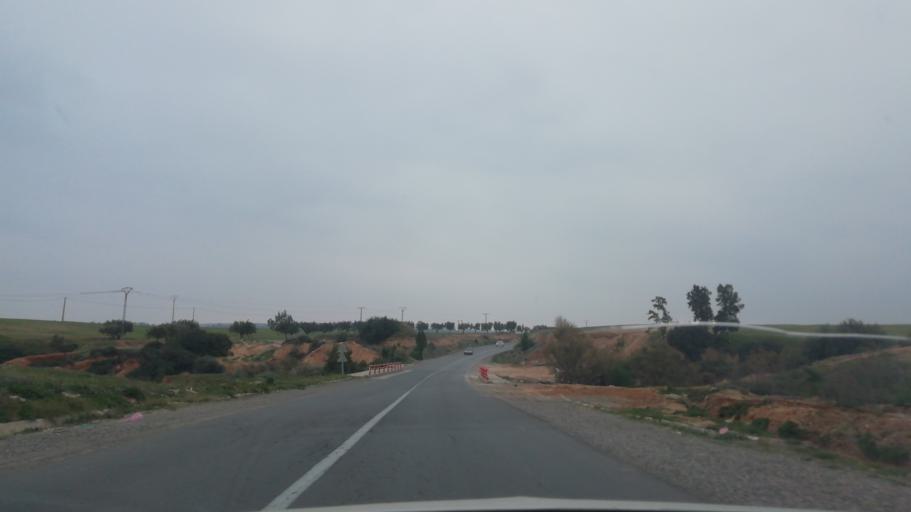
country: DZ
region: Sidi Bel Abbes
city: Sfizef
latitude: 35.2742
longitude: -0.1553
